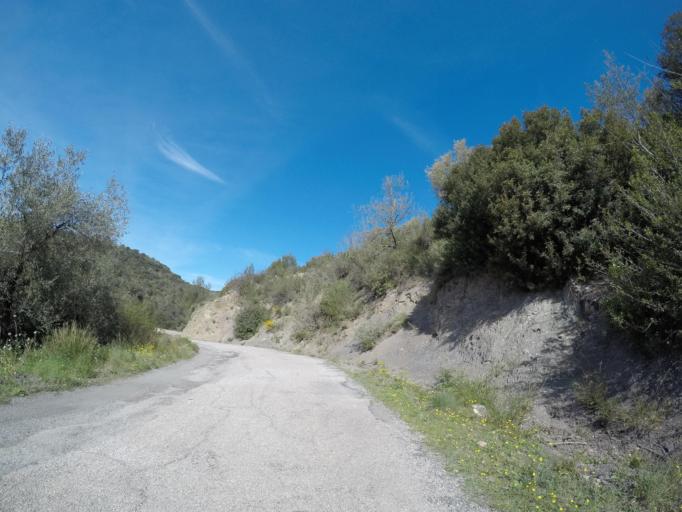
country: FR
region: Languedoc-Roussillon
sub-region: Departement des Pyrenees-Orientales
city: Thuir
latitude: 42.6289
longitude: 2.7040
